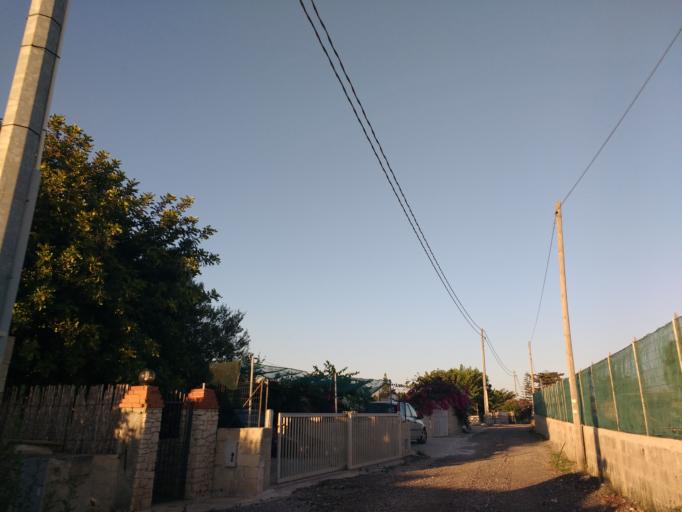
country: IT
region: Sicily
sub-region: Ragusa
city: Ispica
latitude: 36.7281
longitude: 14.9177
